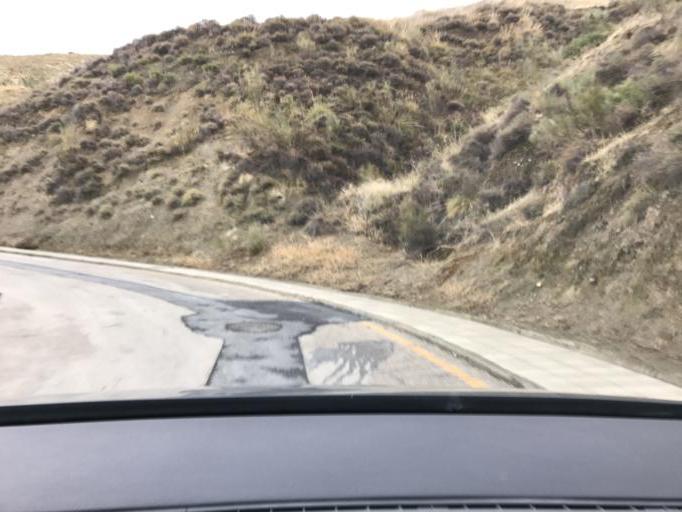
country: ES
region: Andalusia
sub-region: Provincia de Granada
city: Cenes de la Vega
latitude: 37.1654
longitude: -3.5425
